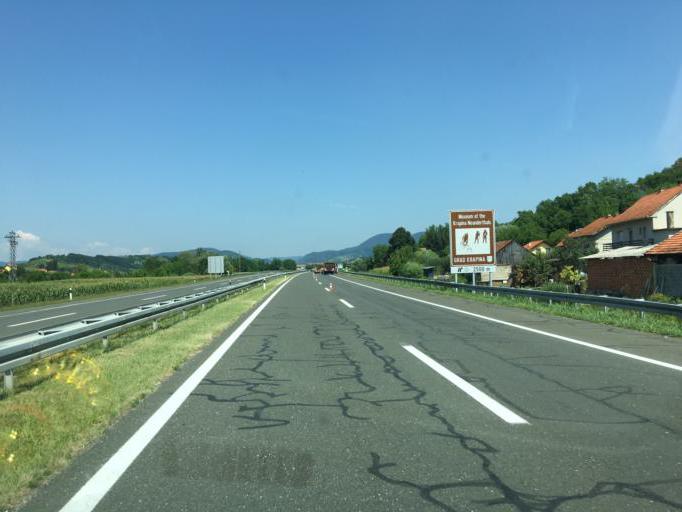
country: HR
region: Krapinsko-Zagorska
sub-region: Grad Krapina
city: Krapina
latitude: 46.1084
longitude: 15.8939
